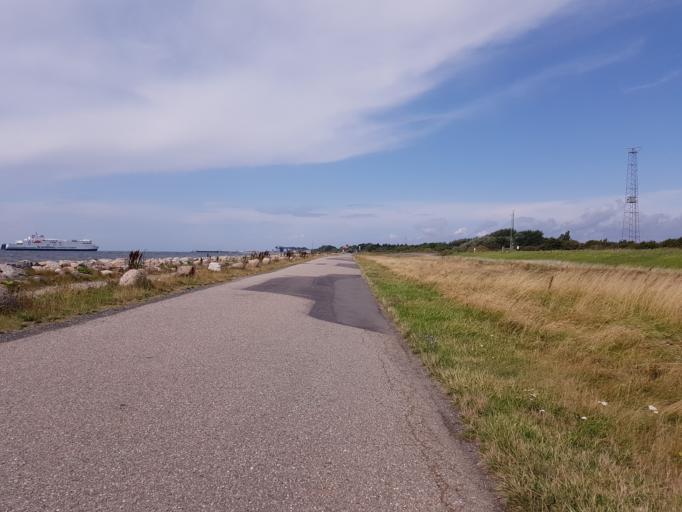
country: DK
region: Zealand
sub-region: Guldborgsund Kommune
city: Nykobing Falster
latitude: 54.5677
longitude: 11.9450
